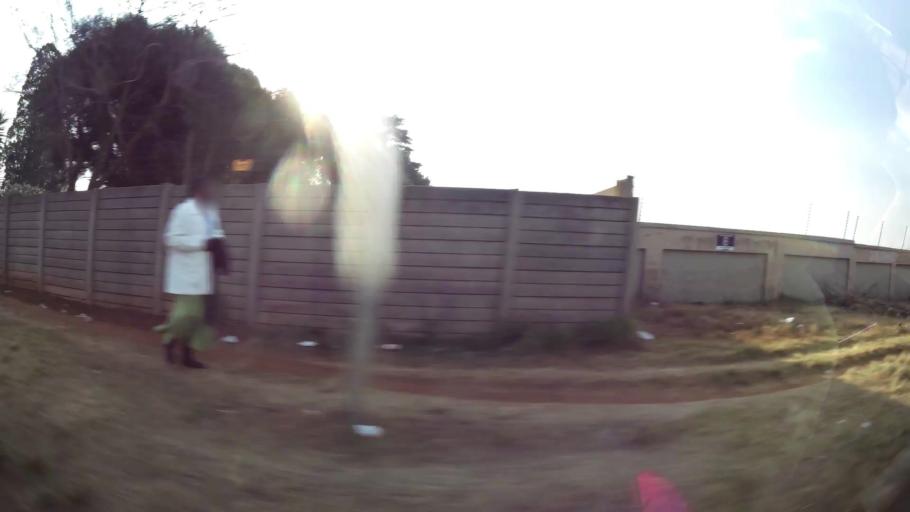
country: ZA
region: Gauteng
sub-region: Ekurhuleni Metropolitan Municipality
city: Benoni
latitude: -26.1120
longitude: 28.2918
